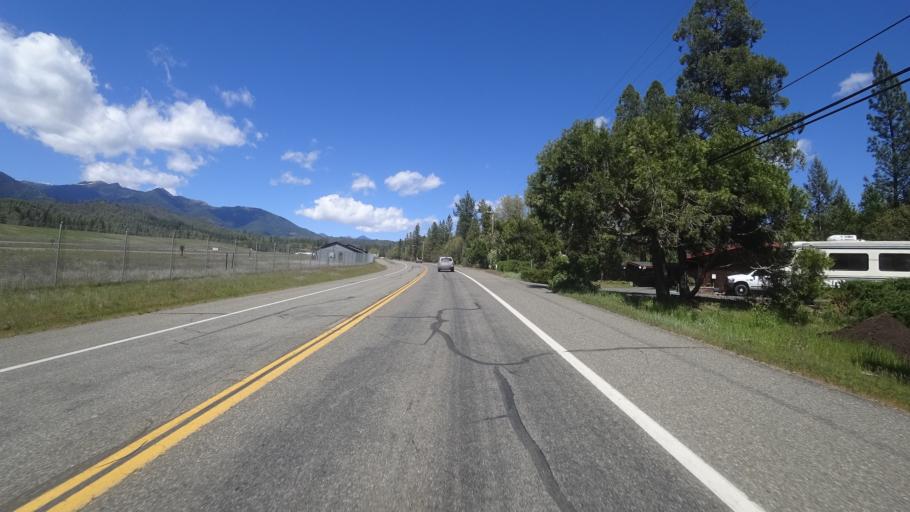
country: US
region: California
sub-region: Trinity County
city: Weaverville
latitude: 40.7430
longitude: -122.9233
